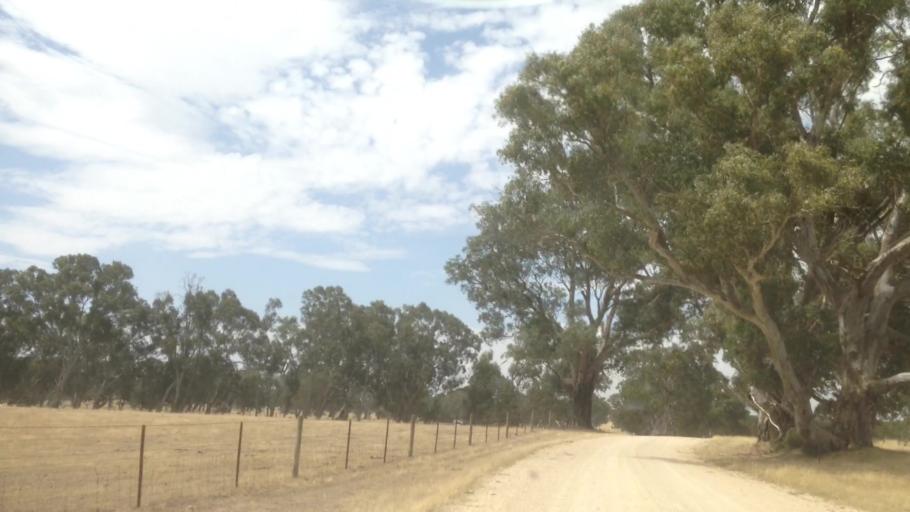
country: AU
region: South Australia
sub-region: Barossa
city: Williamstown
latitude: -34.6926
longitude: 138.9926
